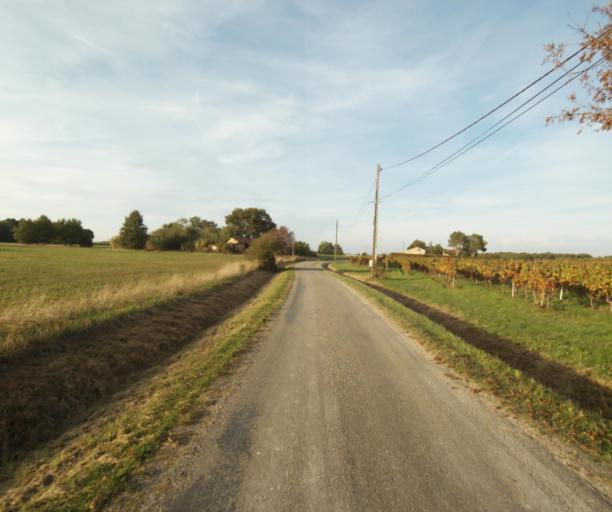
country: FR
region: Midi-Pyrenees
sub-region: Departement du Tarn-et-Garonne
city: Campsas
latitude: 43.8931
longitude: 1.3468
